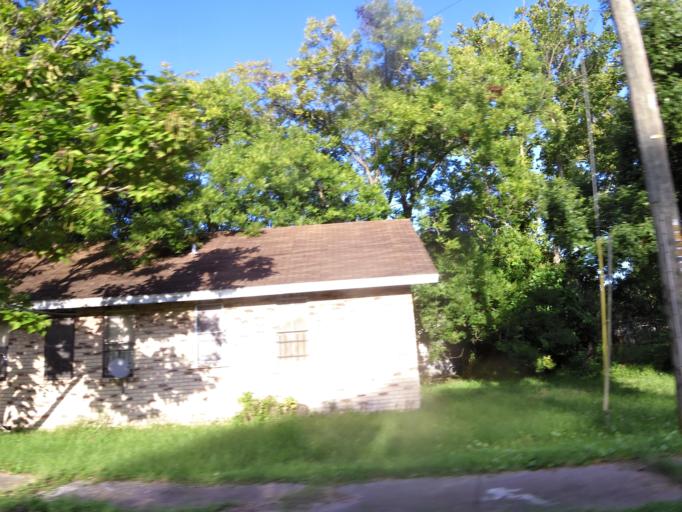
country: US
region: Florida
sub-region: Duval County
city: Jacksonville
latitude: 30.3414
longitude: -81.6929
